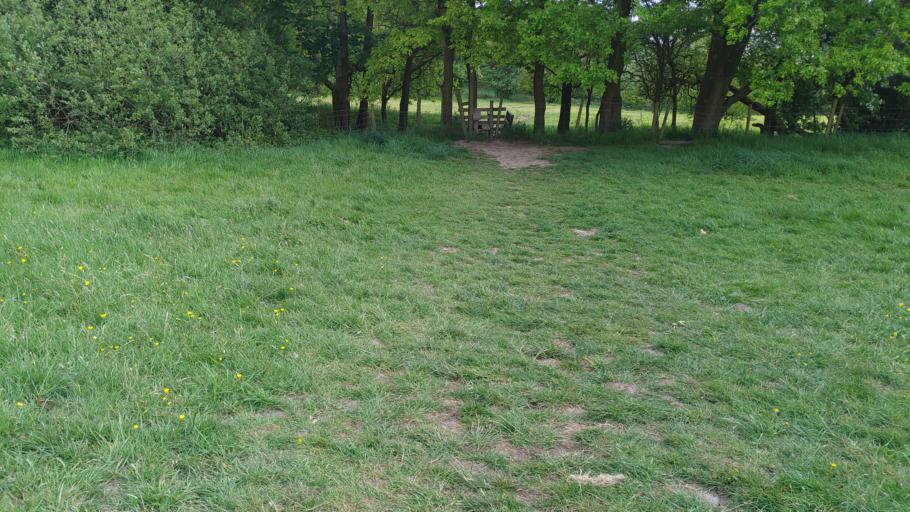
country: GB
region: England
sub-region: Lancashire
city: Chorley
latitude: 53.6691
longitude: -2.6066
